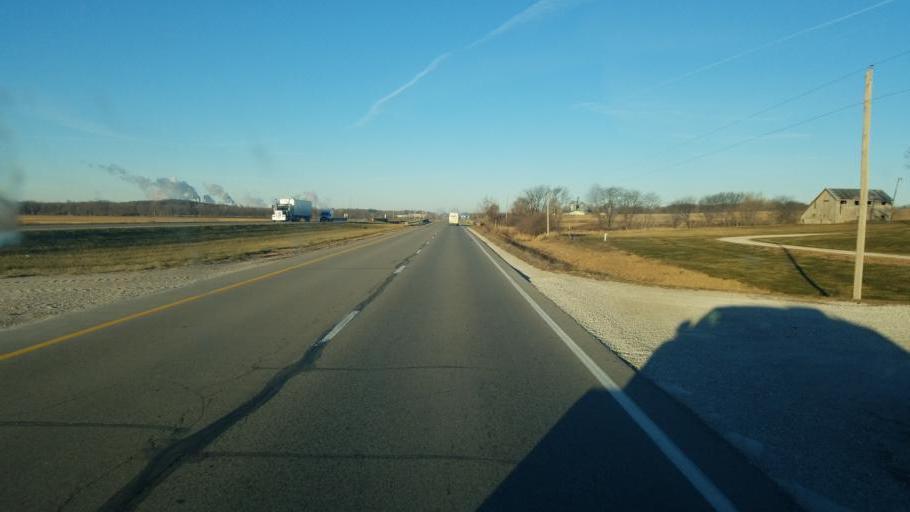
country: US
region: Iowa
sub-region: Wapello County
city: Eddyville
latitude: 41.1405
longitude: -92.6028
